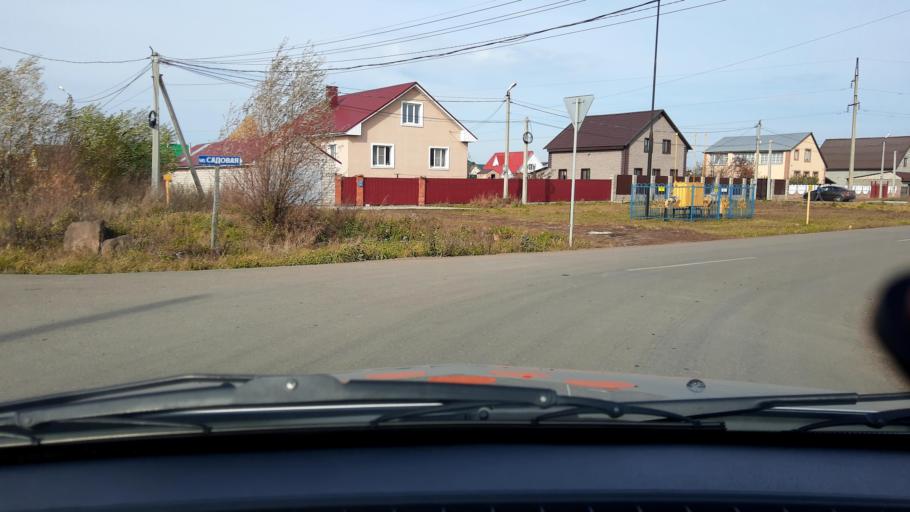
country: RU
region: Bashkortostan
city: Mikhaylovka
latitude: 54.7875
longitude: 55.8285
